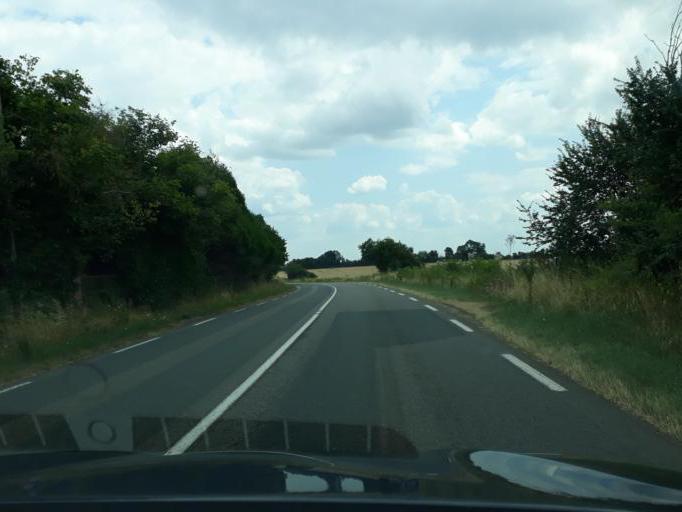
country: FR
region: Centre
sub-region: Departement du Cher
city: Avord
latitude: 47.0214
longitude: 2.6838
